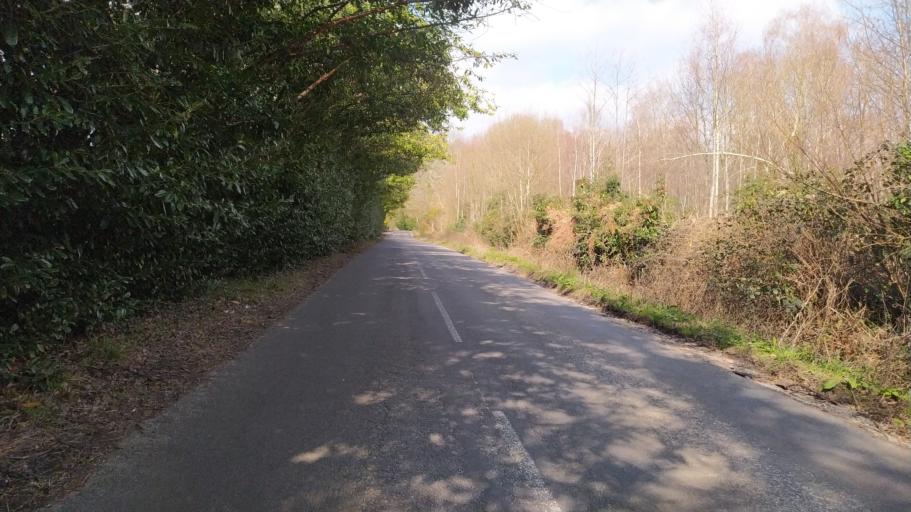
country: GB
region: England
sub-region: Hampshire
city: West Wellow
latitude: 50.9899
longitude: -1.5508
